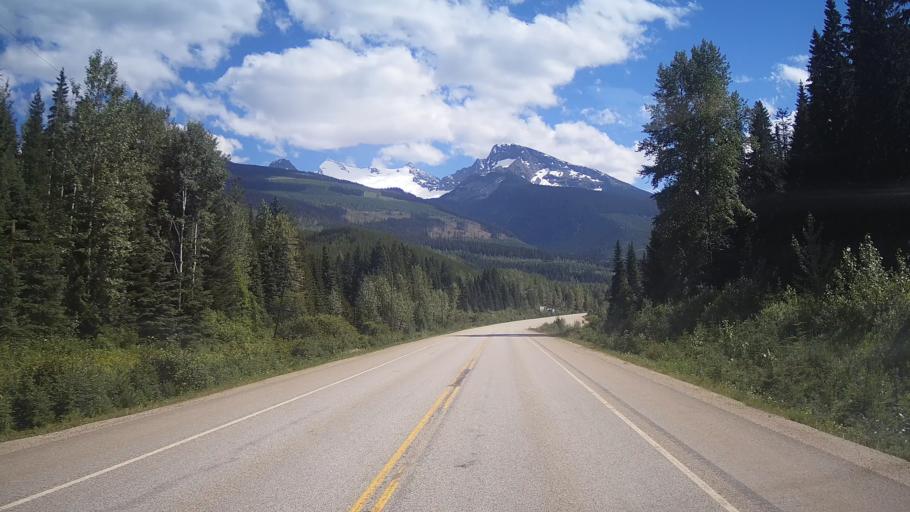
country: CA
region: Alberta
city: Jasper Park Lodge
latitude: 52.5890
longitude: -119.0976
